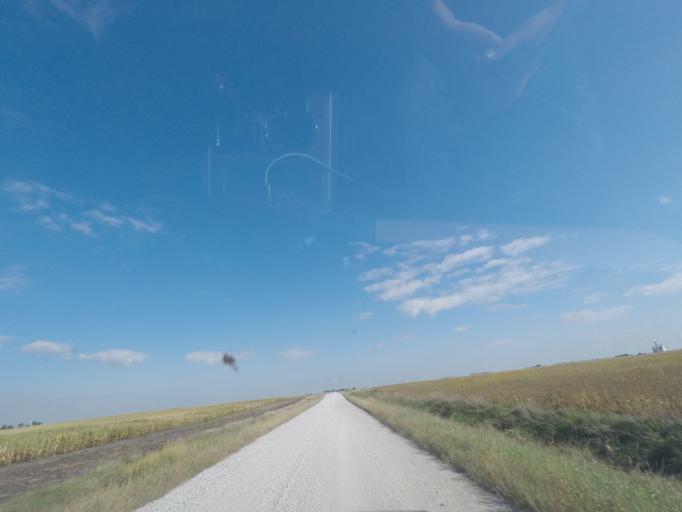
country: US
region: Iowa
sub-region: Story County
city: Nevada
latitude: 42.0375
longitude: -93.4252
